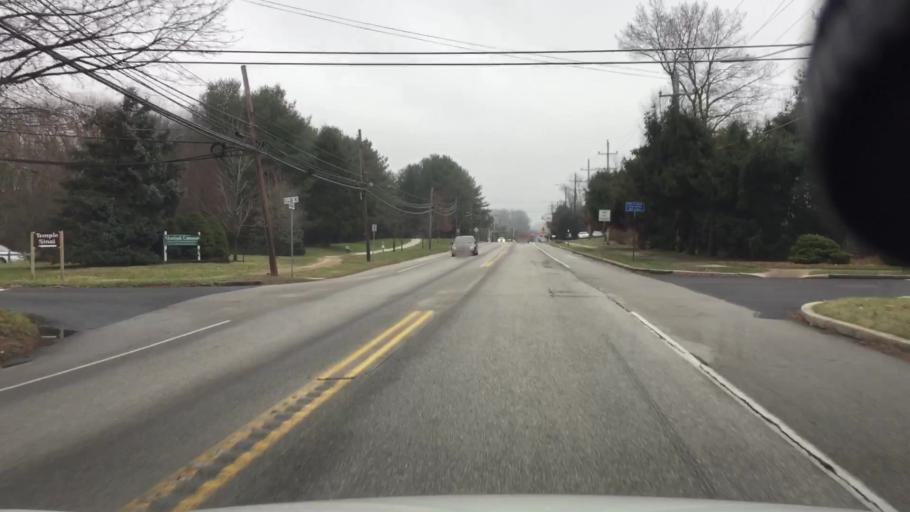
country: US
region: Pennsylvania
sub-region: Montgomery County
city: Dresher
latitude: 40.1527
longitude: -75.1864
